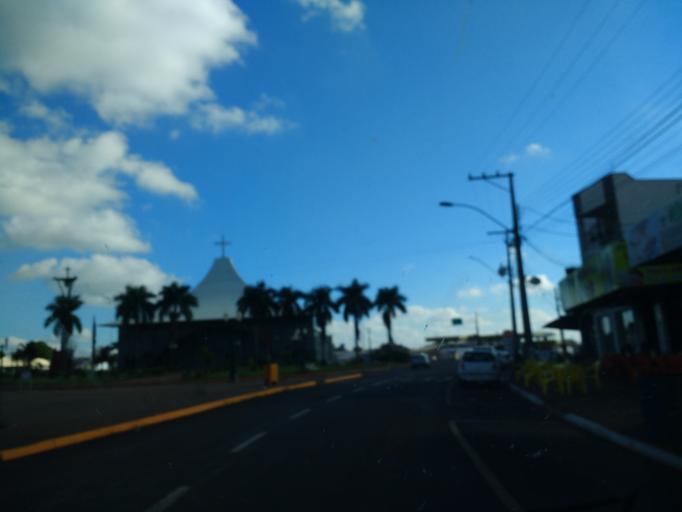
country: BR
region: Parana
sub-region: Palotina
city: Palotina
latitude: -24.4108
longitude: -53.5214
